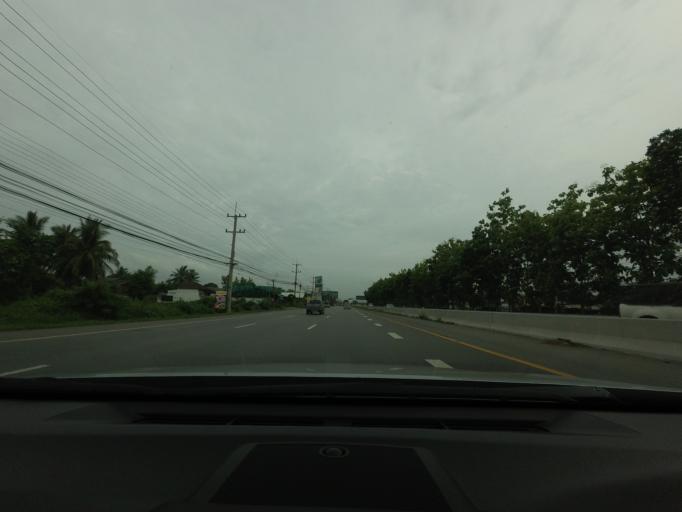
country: TH
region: Ratchaburi
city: Pak Tho
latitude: 13.3203
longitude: 99.8277
